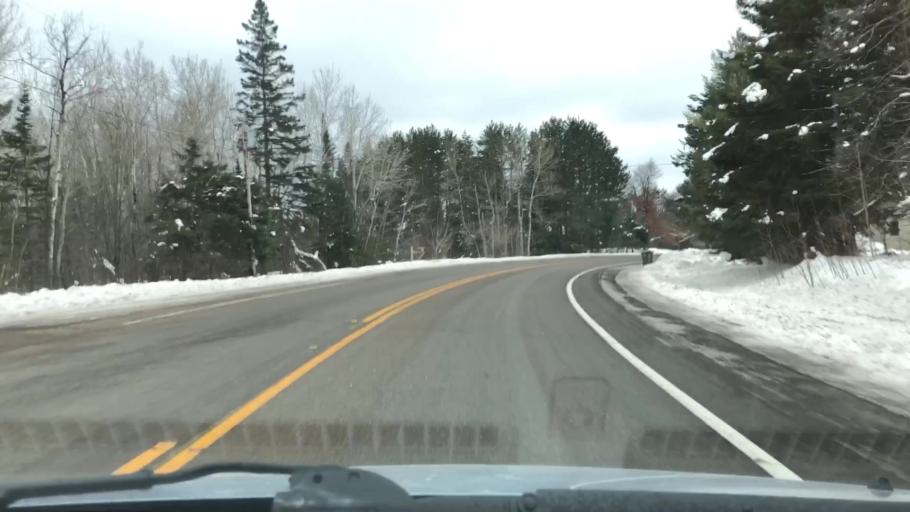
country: US
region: Minnesota
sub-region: Carlton County
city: Esko
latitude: 46.6850
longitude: -92.3649
